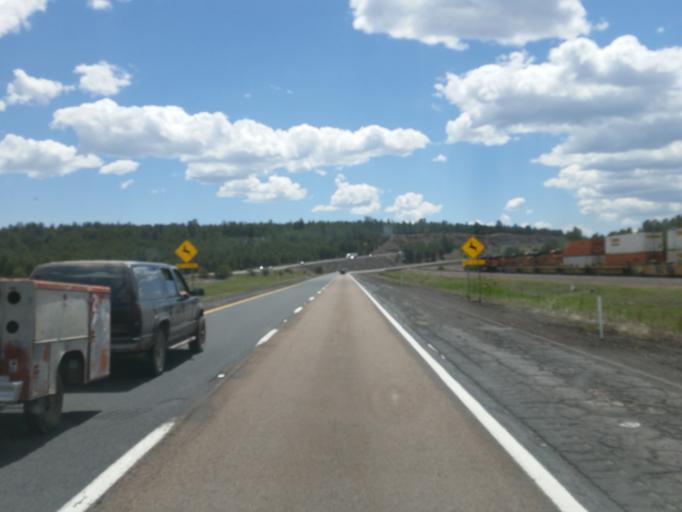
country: US
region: Arizona
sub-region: Coconino County
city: Flagstaff
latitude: 35.2140
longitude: -111.7804
